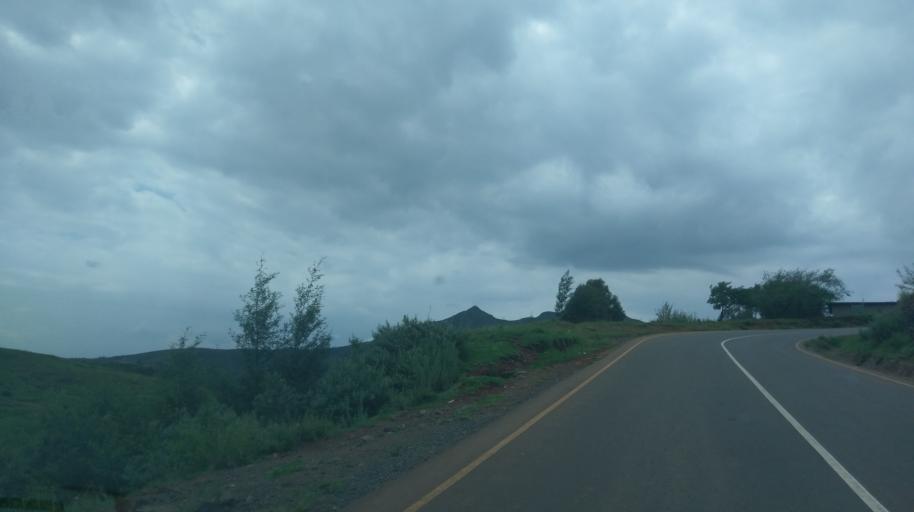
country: LS
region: Butha-Buthe
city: Butha-Buthe
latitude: -29.0369
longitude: 28.2800
